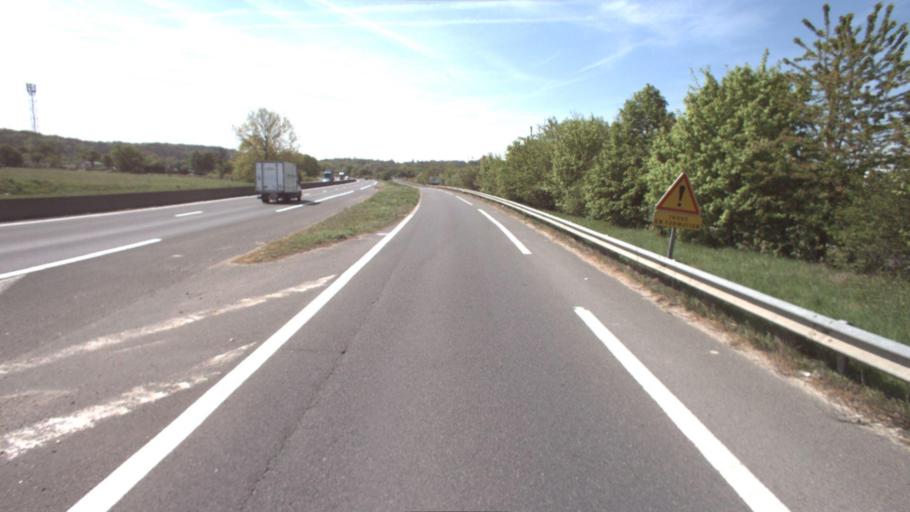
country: FR
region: Ile-de-France
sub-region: Departement de Seine-et-Marne
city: Saint-Mard
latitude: 49.0629
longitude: 2.7054
